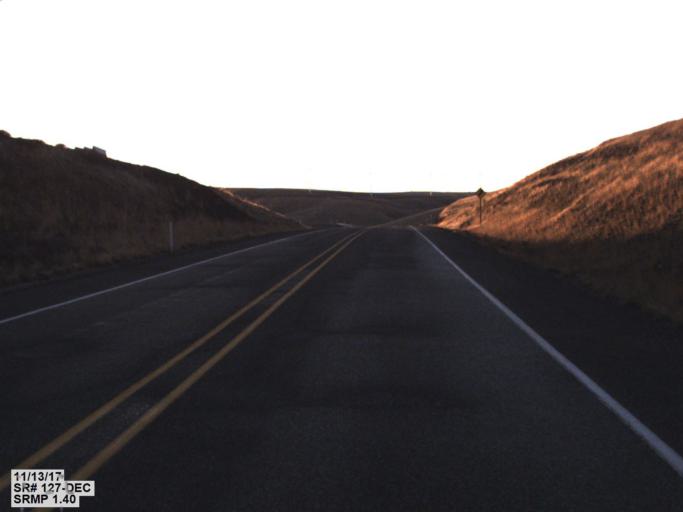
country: US
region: Washington
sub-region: Garfield County
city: Pomeroy
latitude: 46.5257
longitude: -117.7954
